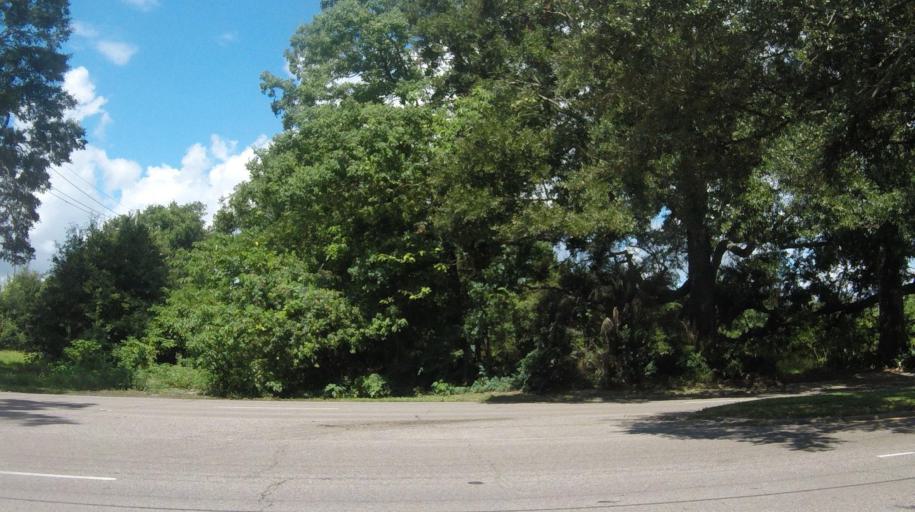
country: US
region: Louisiana
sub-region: West Baton Rouge Parish
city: Port Allen
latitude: 30.4290
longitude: -91.1877
